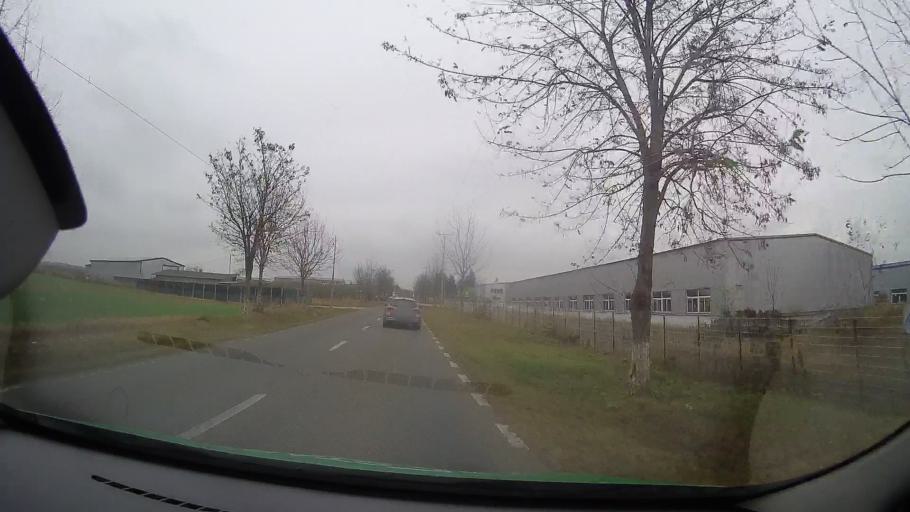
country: RO
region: Prahova
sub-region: Oras Baicoi
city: Liliesti
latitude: 45.0148
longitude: 25.8850
